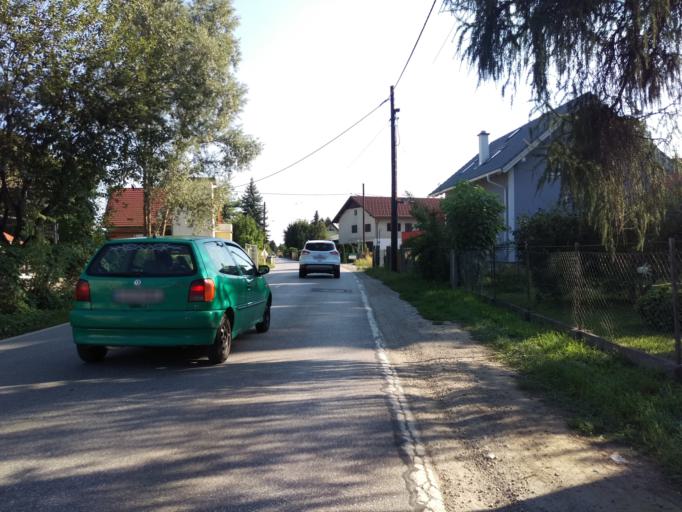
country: AT
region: Styria
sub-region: Politischer Bezirk Graz-Umgebung
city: Feldkirchen bei Graz
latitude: 47.0302
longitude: 15.4417
